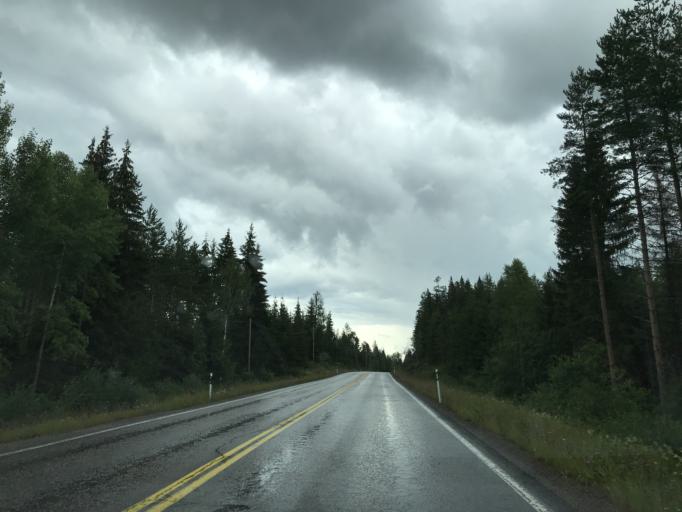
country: FI
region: Uusimaa
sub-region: Porvoo
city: Pukkila
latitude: 60.7796
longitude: 25.5779
